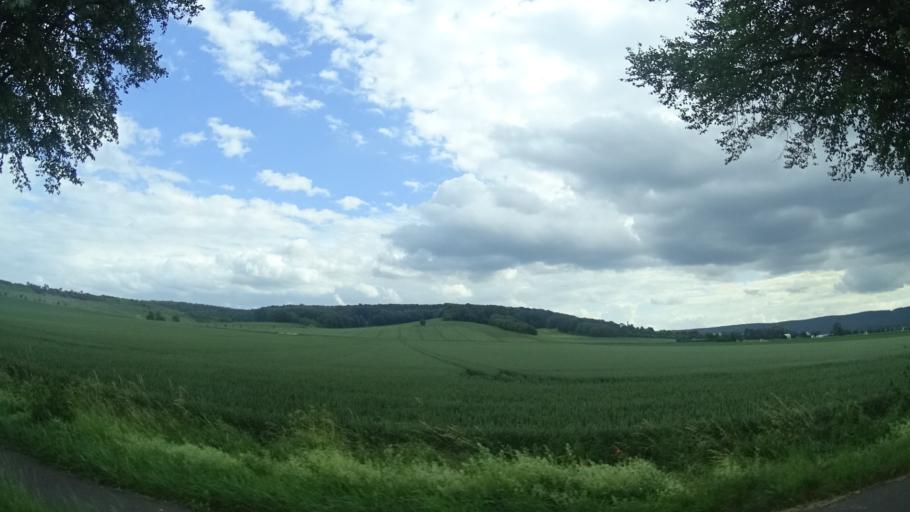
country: DE
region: Lower Saxony
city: Giesen
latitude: 52.1595
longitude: 9.8945
